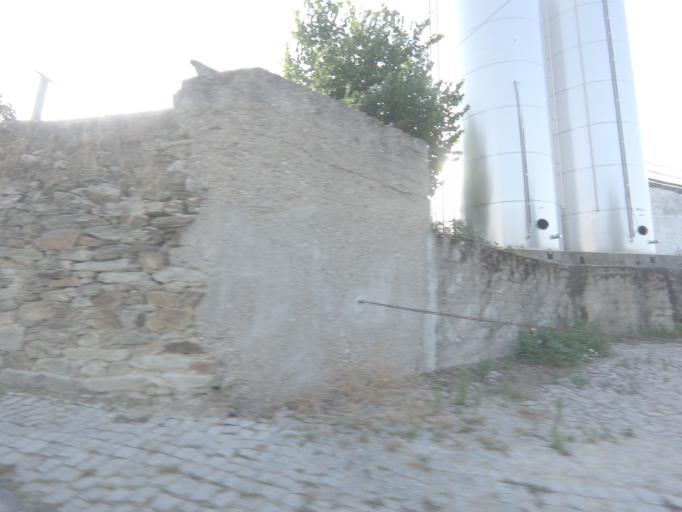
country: PT
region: Viseu
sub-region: Sao Joao da Pesqueira
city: Sao Joao da Pesqueira
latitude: 41.2251
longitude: -7.4663
